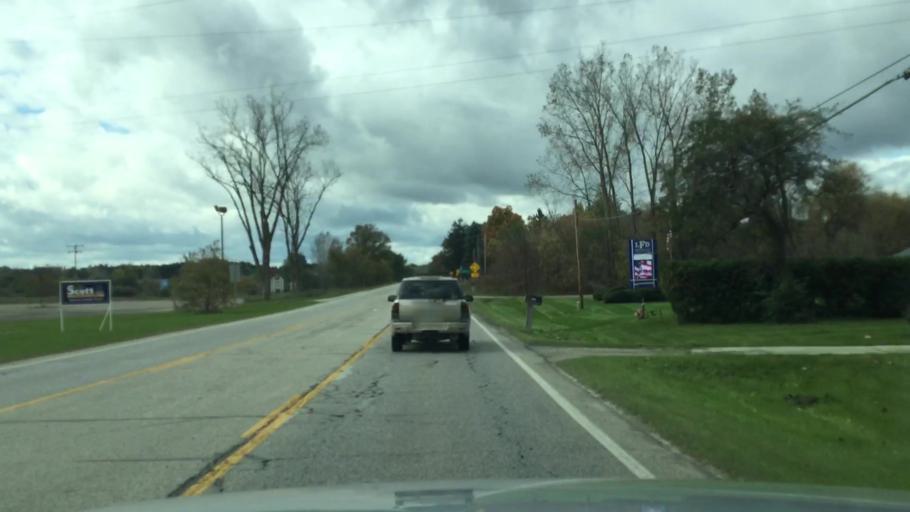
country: US
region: Michigan
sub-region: Lapeer County
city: Lapeer
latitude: 43.0453
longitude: -83.3570
